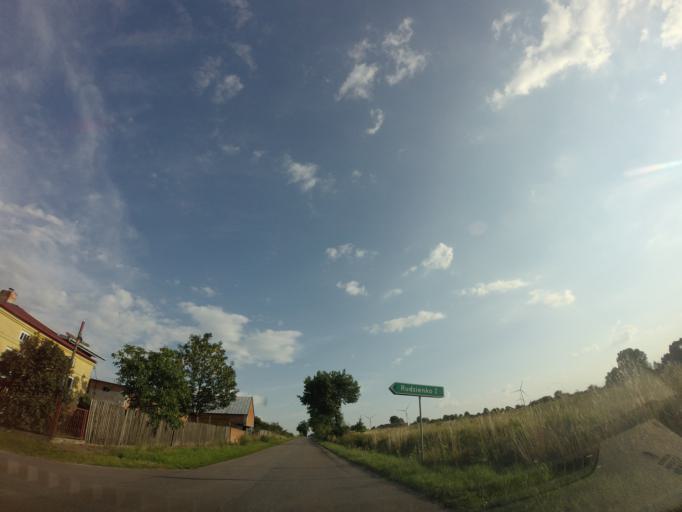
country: PL
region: Lublin Voivodeship
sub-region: Powiat lubartowski
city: Michow
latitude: 51.5173
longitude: 22.3110
